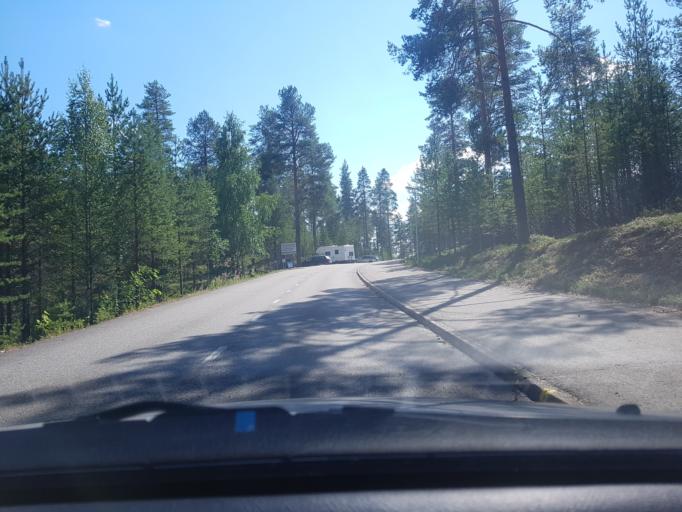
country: FI
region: Kainuu
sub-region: Kehys-Kainuu
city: Kuhmo
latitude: 64.1176
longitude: 29.5871
